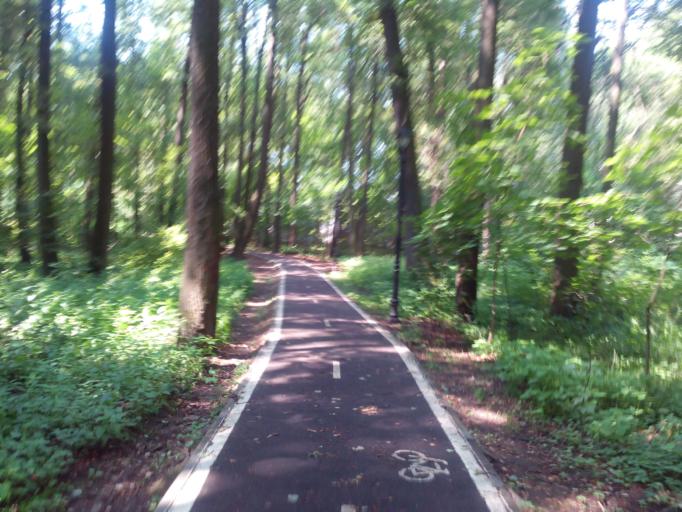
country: RU
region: Moskovskaya
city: Fili
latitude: 55.7525
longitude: 37.4818
